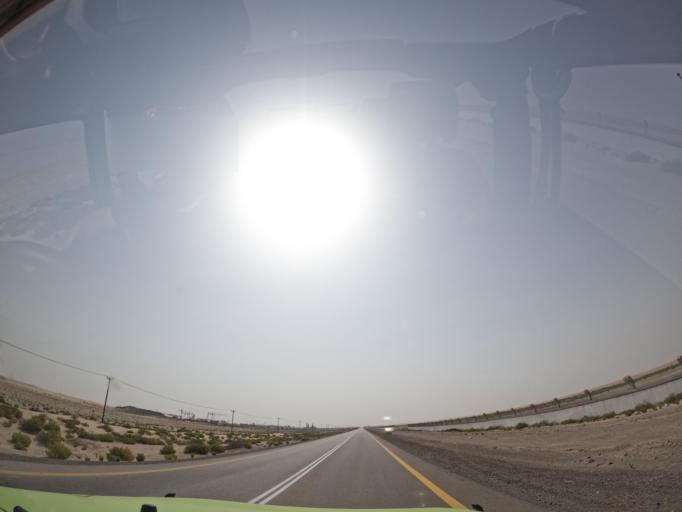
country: AE
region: Dubai
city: Dubai
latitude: 24.6780
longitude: 55.1488
